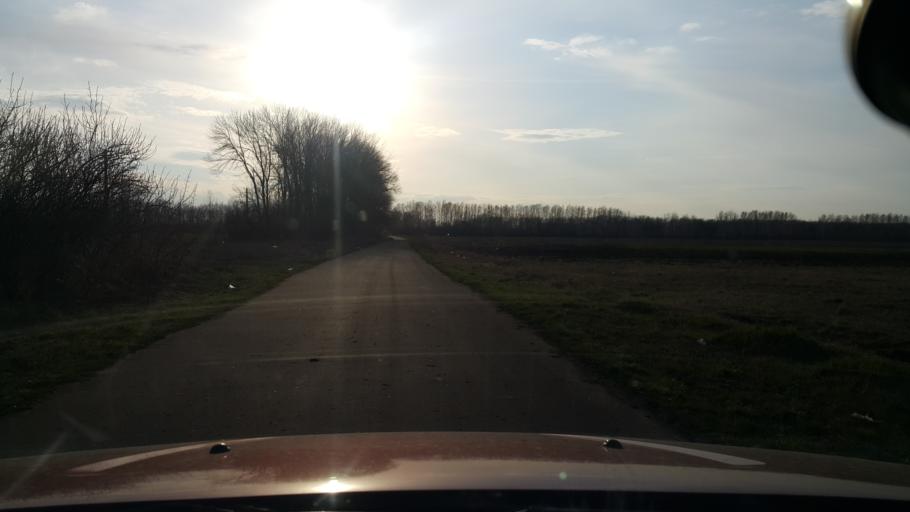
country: RU
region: Tambov
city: Kotovsk
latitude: 52.5901
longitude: 41.4559
